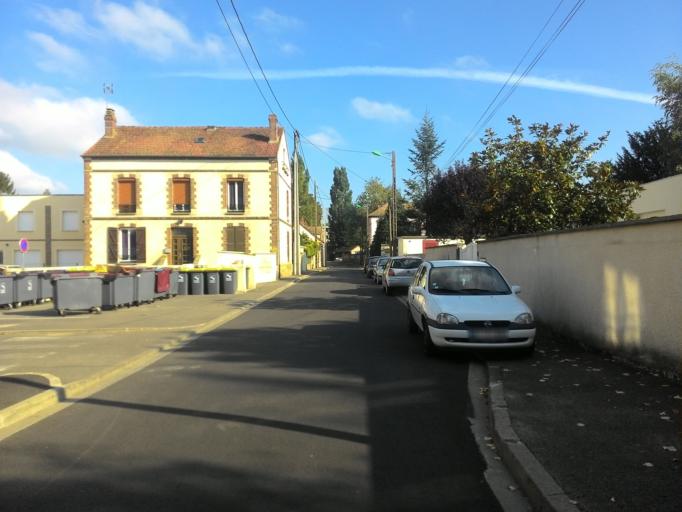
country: FR
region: Bourgogne
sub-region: Departement de l'Yonne
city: Sens
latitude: 48.1927
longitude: 3.2759
